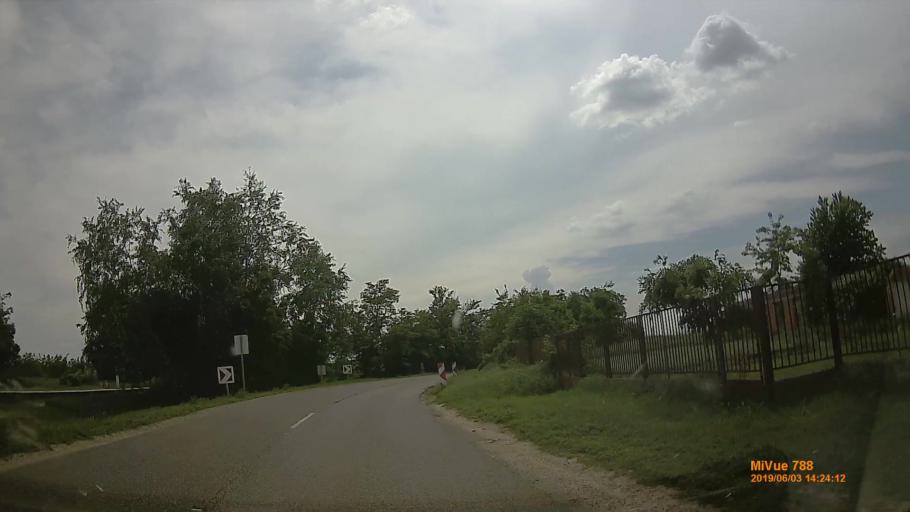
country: HU
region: Pest
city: Jaszkarajeno
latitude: 47.0173
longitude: 20.1342
